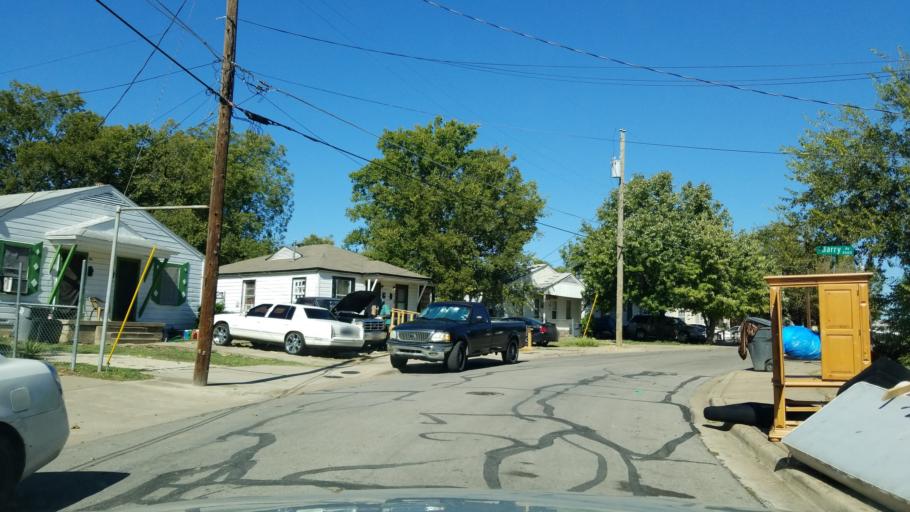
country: US
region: Texas
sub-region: Dallas County
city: Dallas
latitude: 32.7805
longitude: -96.7464
